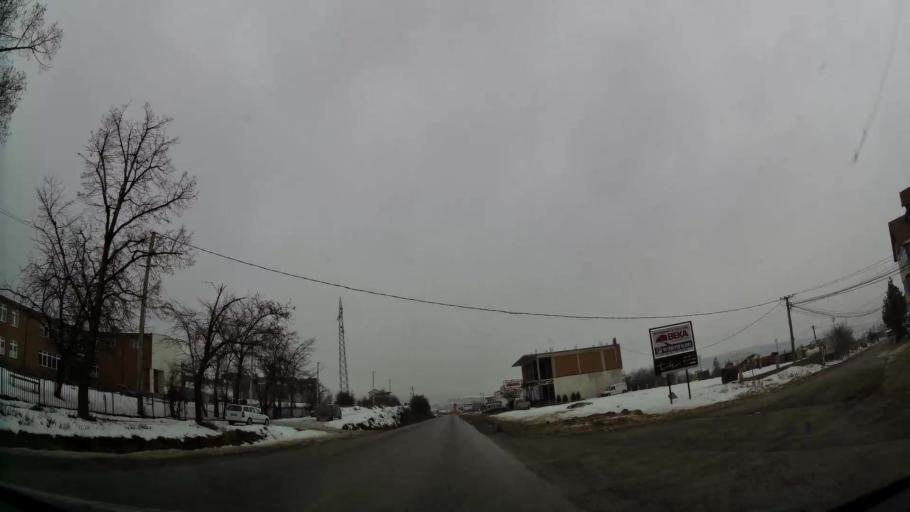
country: XK
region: Pristina
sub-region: Komuna e Prishtines
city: Pristina
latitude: 42.7155
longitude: 21.1499
